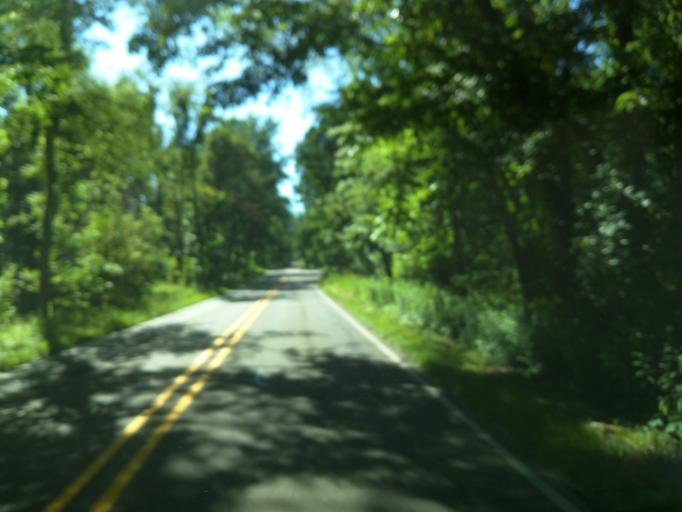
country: US
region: Michigan
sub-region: Ingham County
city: Edgemont Park
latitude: 42.7630
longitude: -84.6095
